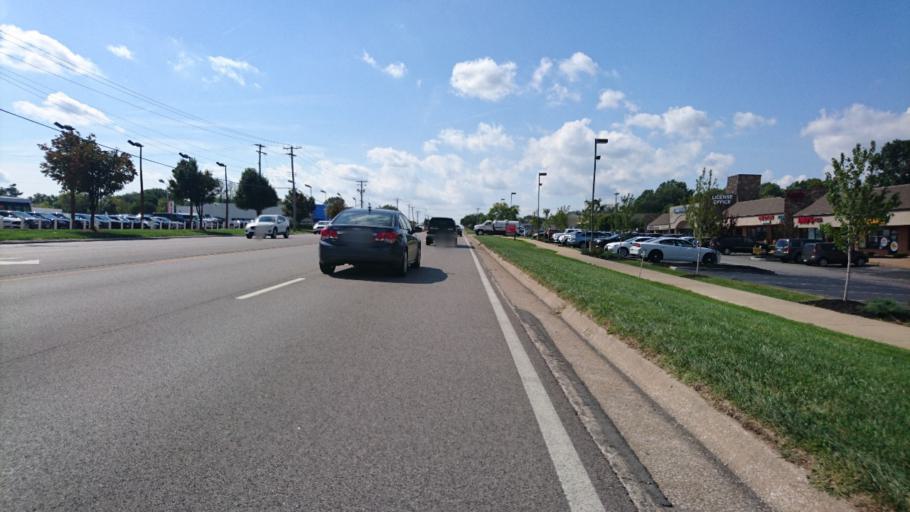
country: US
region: Missouri
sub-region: Saint Louis County
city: Ellisville
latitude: 38.5929
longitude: -90.5683
